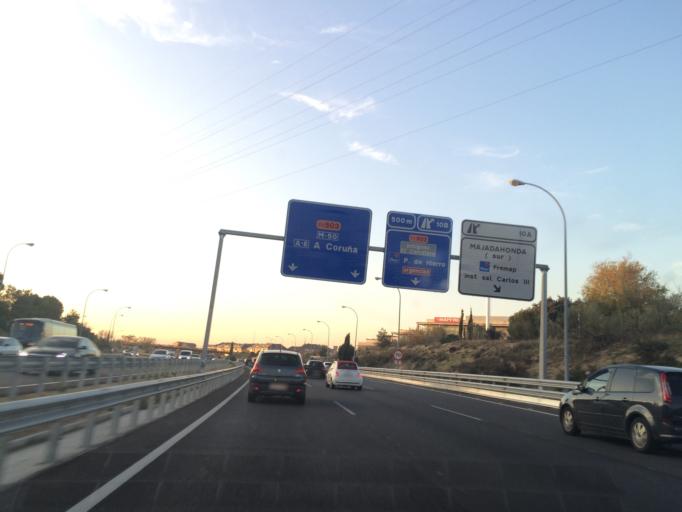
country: ES
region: Madrid
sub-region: Provincia de Madrid
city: Majadahonda
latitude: 40.4472
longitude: -3.8546
